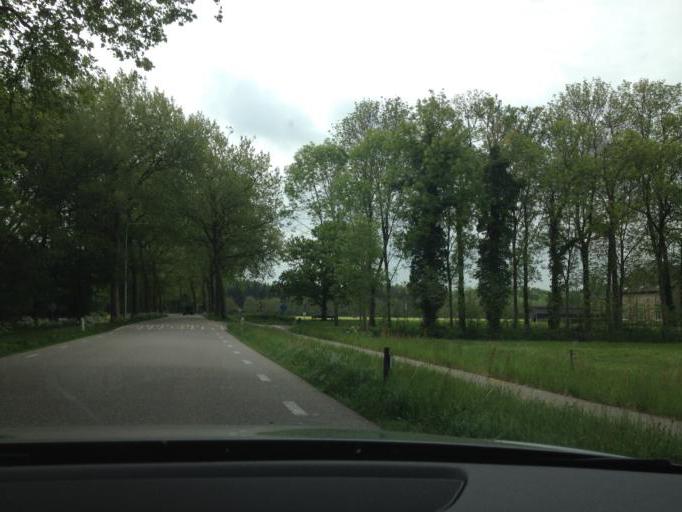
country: NL
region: Gelderland
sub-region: Gemeente Barneveld
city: Terschuur
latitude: 52.1789
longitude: 5.5408
